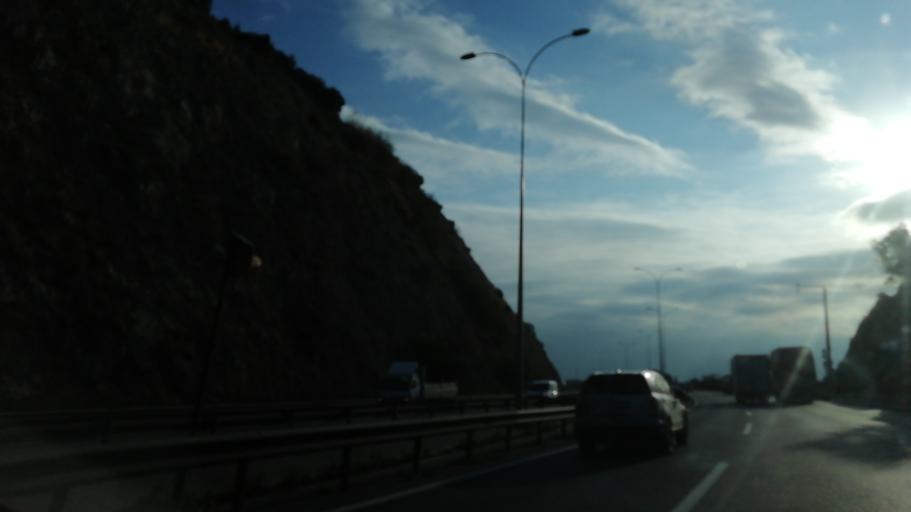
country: TR
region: Kocaeli
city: Hereke
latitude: 40.7782
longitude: 29.6315
